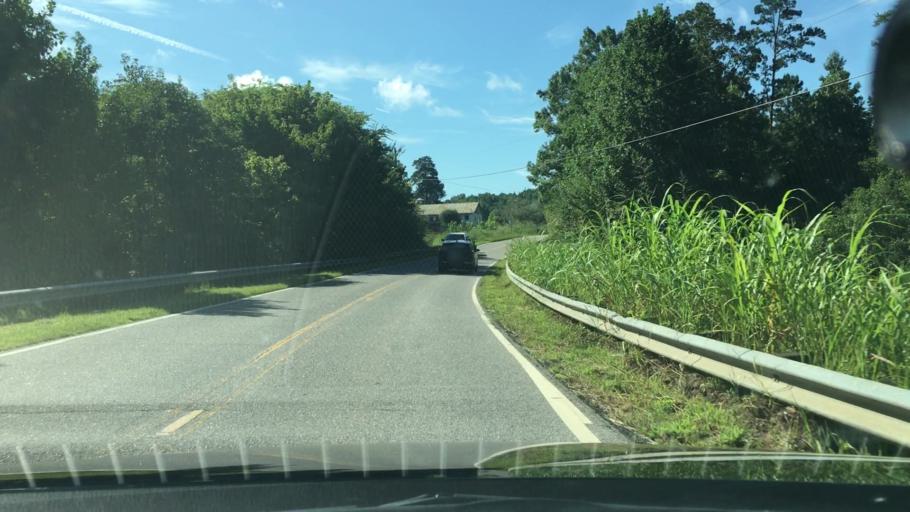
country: US
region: Georgia
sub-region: Putnam County
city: Jefferson
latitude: 33.3892
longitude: -83.2610
